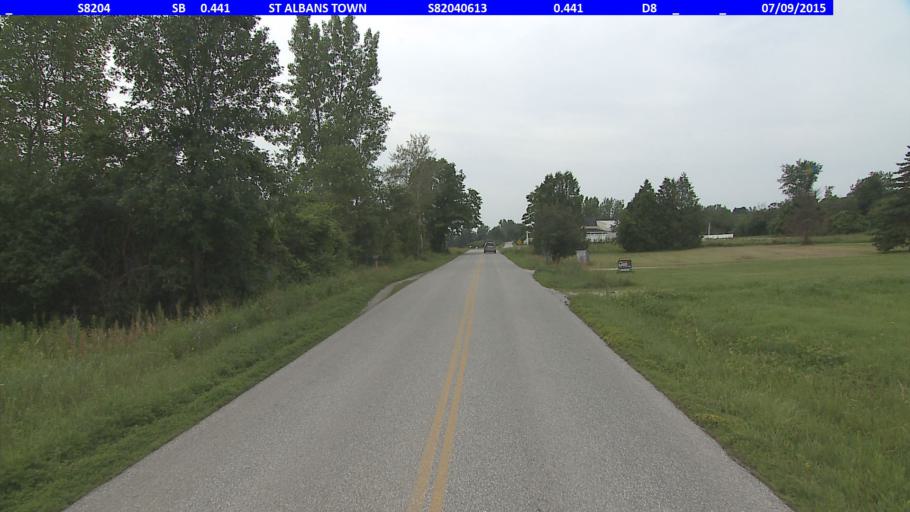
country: US
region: Vermont
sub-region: Franklin County
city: Saint Albans
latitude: 44.8091
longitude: -73.1103
